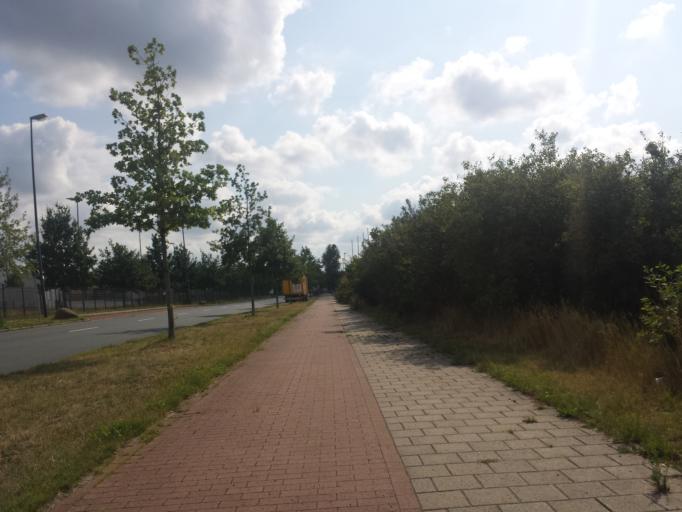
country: DE
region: Lower Saxony
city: Stuhr
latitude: 53.0965
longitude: 8.7019
